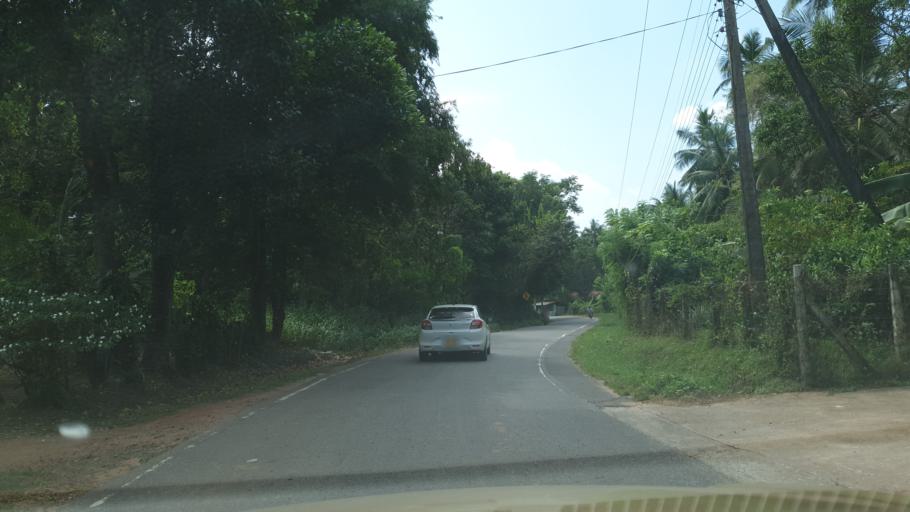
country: LK
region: North Western
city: Kuliyapitiya
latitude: 7.3437
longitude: 79.9862
